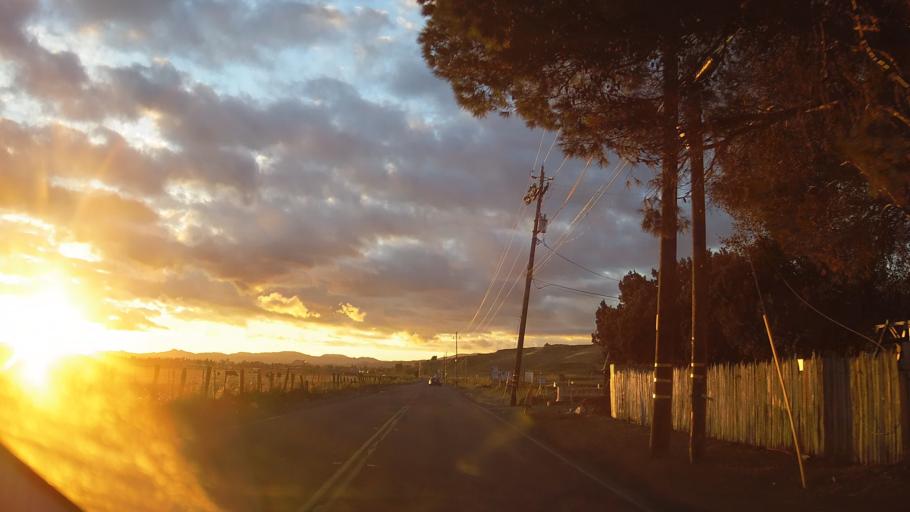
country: US
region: California
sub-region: Solano County
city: Vacaville
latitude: 38.2871
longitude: -121.9791
